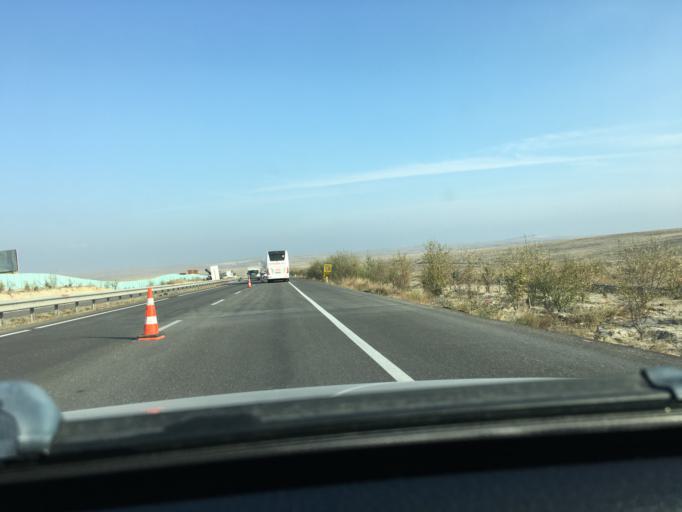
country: TR
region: Eskisehir
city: Gunyuzu
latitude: 39.5743
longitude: 31.8502
